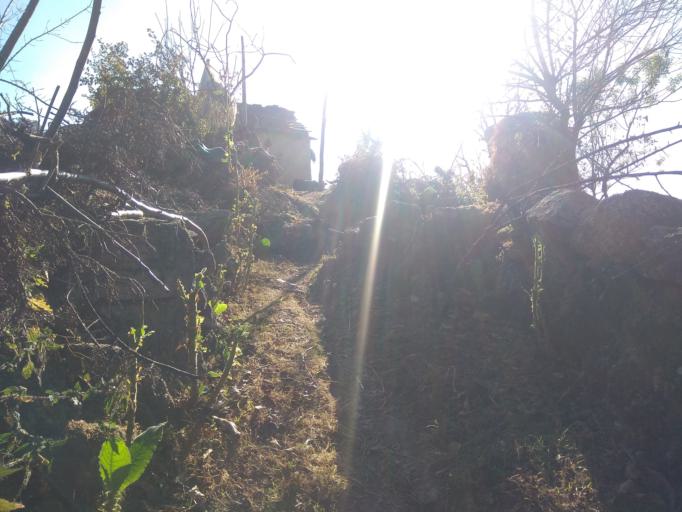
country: NP
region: Far Western
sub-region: Seti Zone
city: Achham
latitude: 29.2761
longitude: 81.6105
